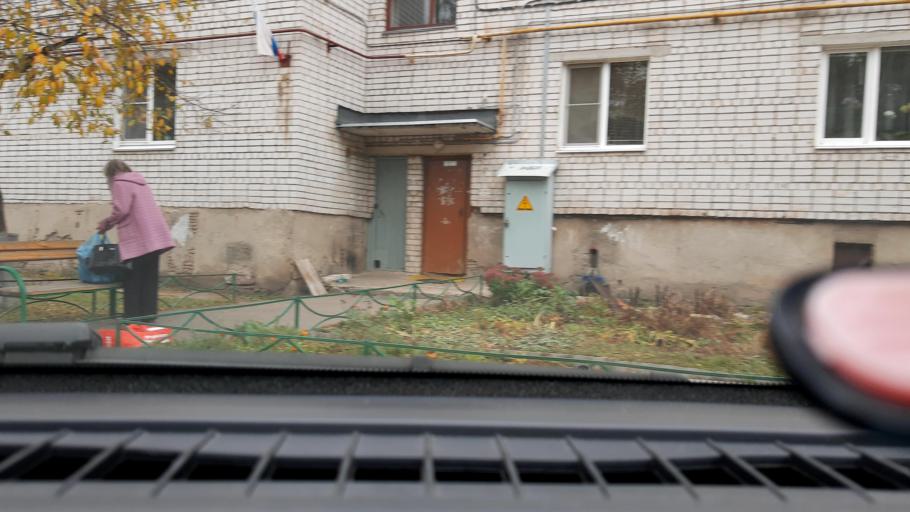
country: RU
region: Nizjnij Novgorod
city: Lukino
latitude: 56.3947
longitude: 43.7213
